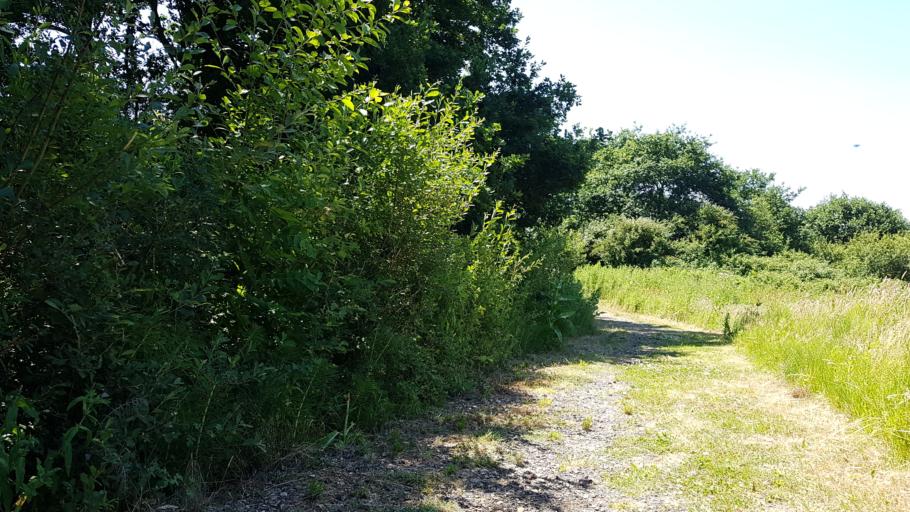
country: GB
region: England
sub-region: Isle of Wight
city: Newport
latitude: 50.6957
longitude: -1.2770
